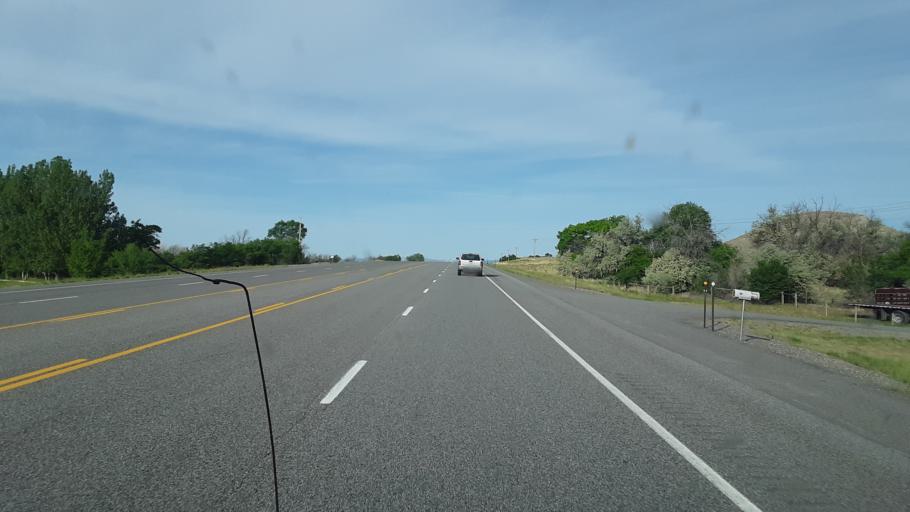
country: US
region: Wyoming
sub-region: Fremont County
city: Riverton
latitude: 43.1248
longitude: -108.3156
